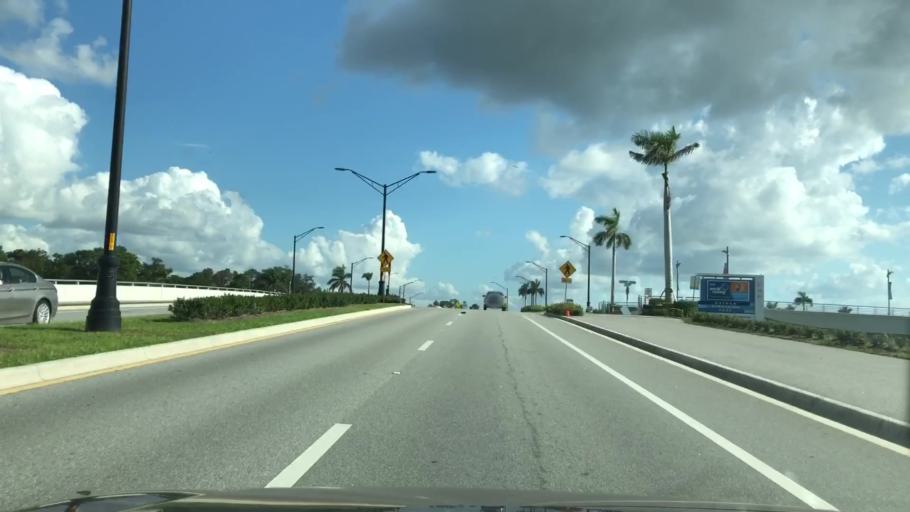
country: US
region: Florida
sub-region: Sarasota County
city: The Meadows
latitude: 27.3771
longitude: -82.4514
